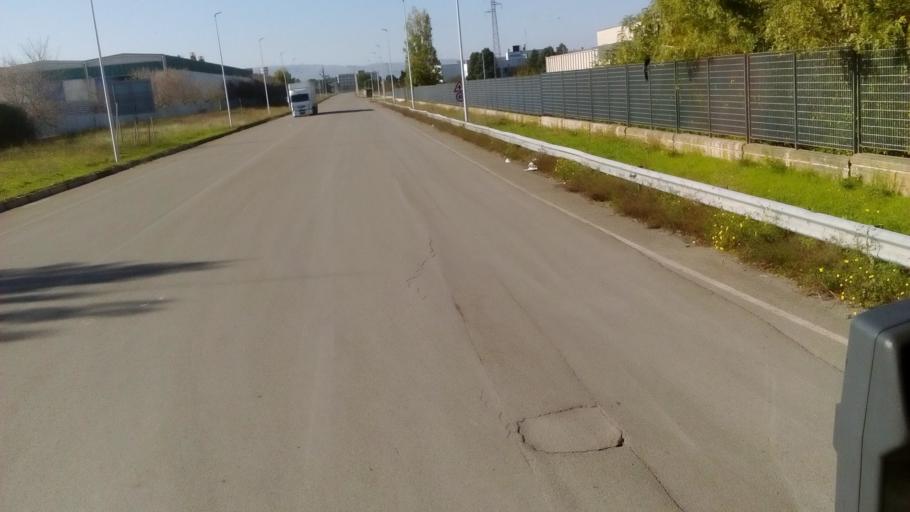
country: IT
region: Basilicate
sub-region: Provincia di Potenza
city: Melfi
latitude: 41.0758
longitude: 15.6854
